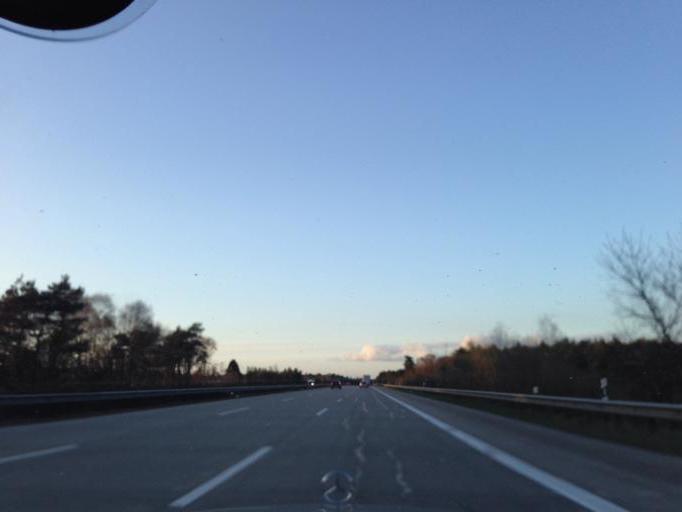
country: DE
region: Lower Saxony
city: Bispingen
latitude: 53.0568
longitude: 9.9540
